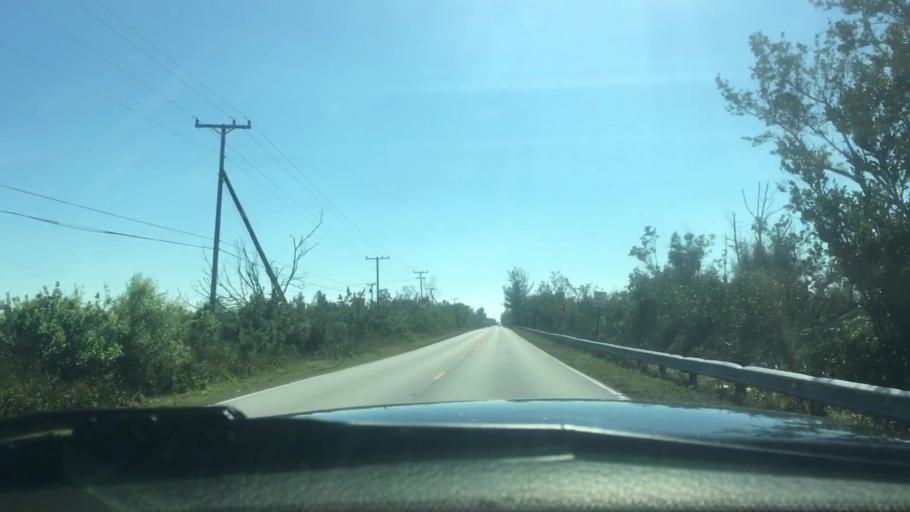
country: US
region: Florida
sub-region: Miami-Dade County
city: Florida City
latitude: 25.3740
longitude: -80.4344
